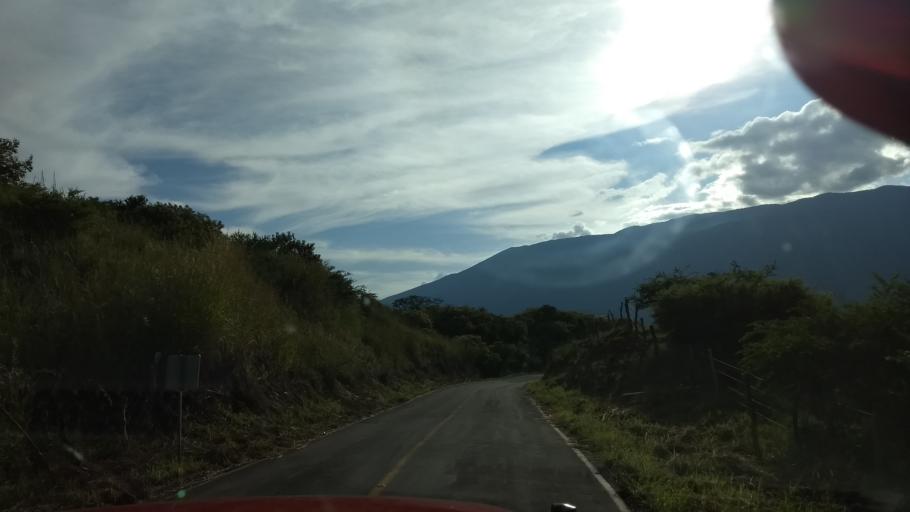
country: MX
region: Colima
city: Suchitlan
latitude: 19.4595
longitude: -103.7943
